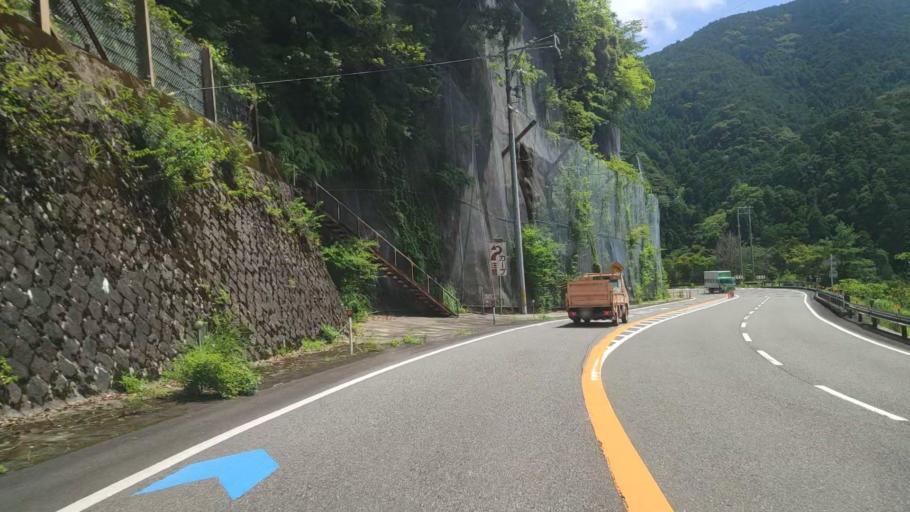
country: JP
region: Mie
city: Owase
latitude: 33.9193
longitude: 136.1026
